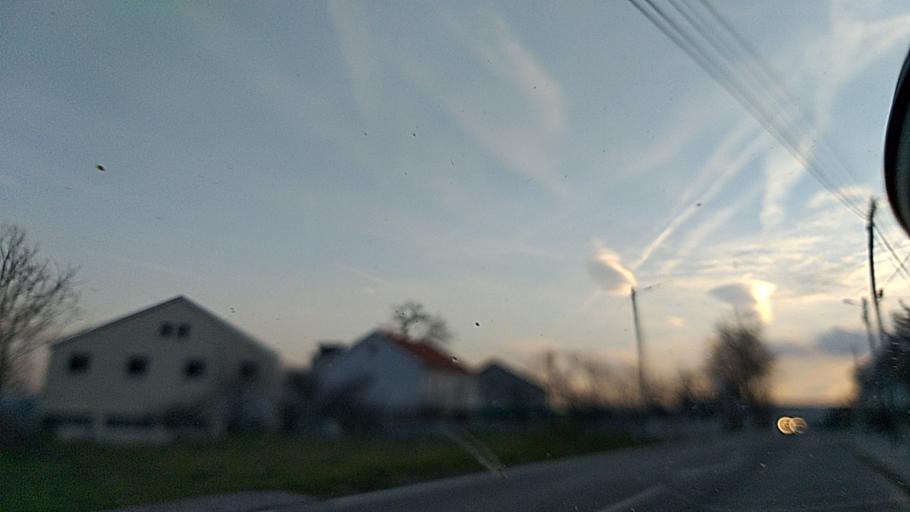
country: PT
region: Guarda
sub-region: Guarda
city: Sequeira
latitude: 40.5763
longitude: -7.1795
